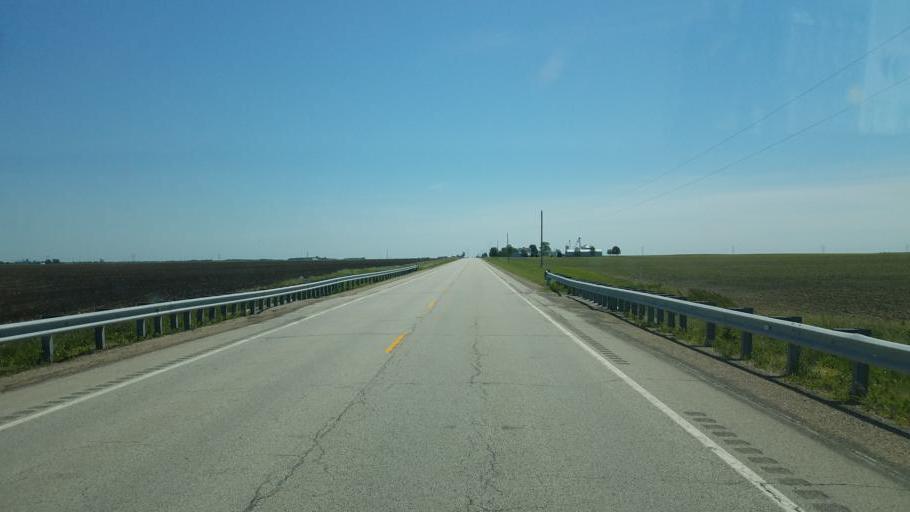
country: US
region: Illinois
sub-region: McLean County
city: Downs
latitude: 40.3121
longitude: -88.8526
